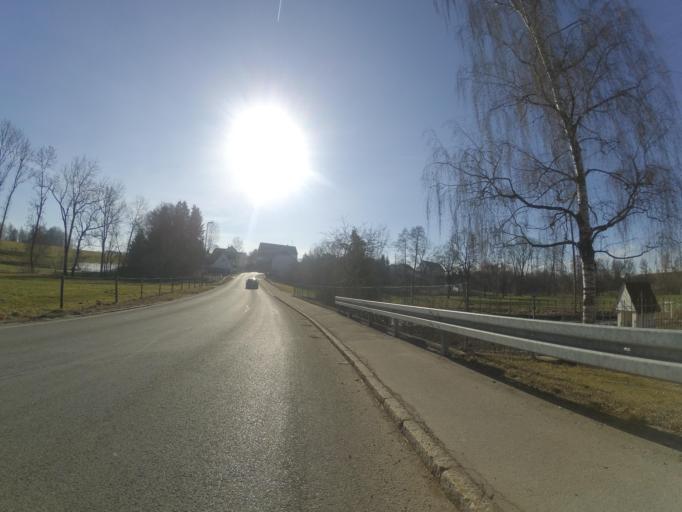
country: DE
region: Baden-Wuerttemberg
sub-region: Tuebingen Region
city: Aulendorf
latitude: 47.9324
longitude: 9.6399
